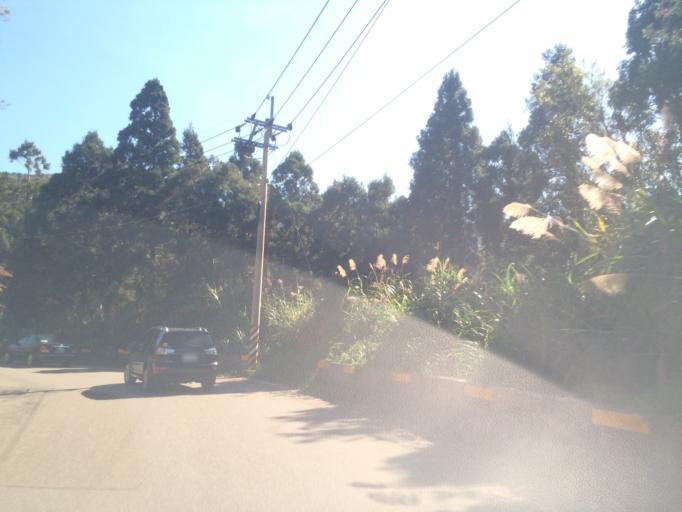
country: TW
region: Taiwan
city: Lugu
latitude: 23.6546
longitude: 120.7839
